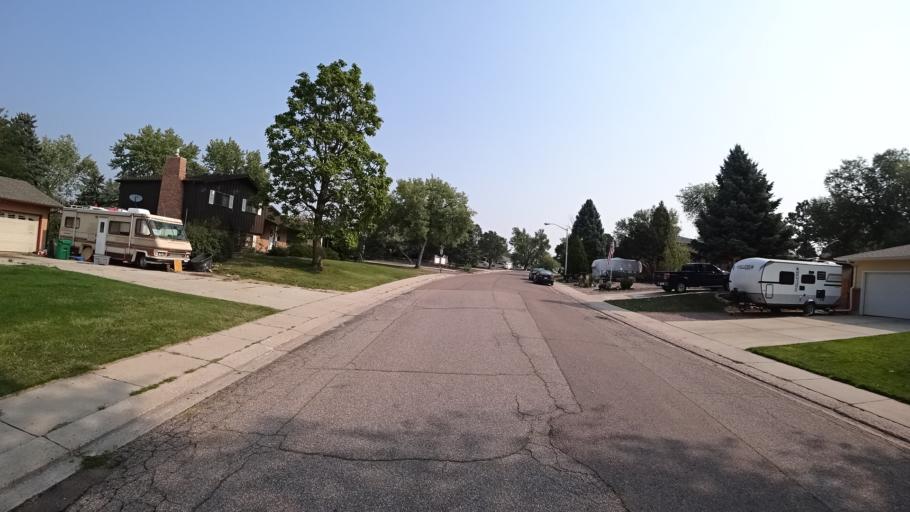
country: US
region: Colorado
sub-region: El Paso County
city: Stratmoor
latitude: 38.8123
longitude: -104.7697
